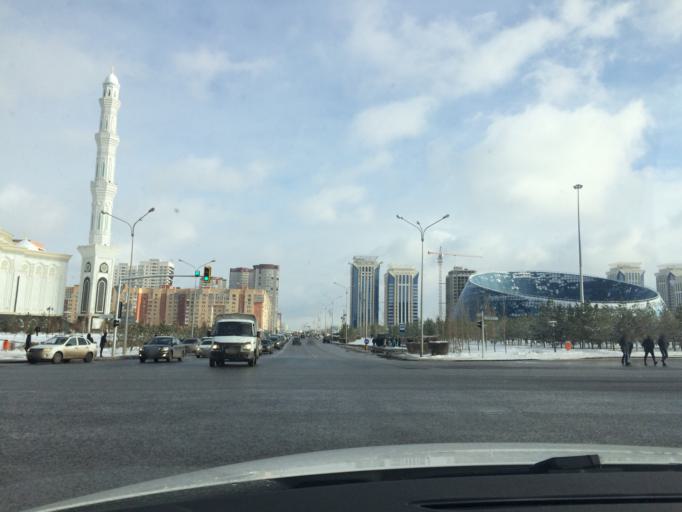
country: KZ
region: Astana Qalasy
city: Astana
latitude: 51.1247
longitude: 71.4690
